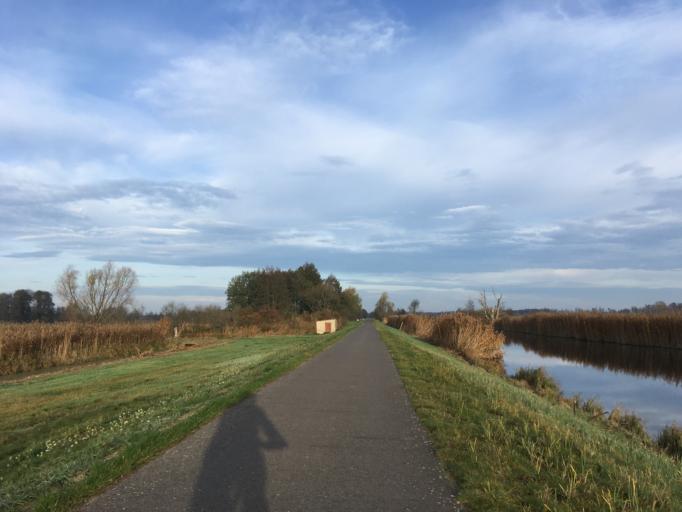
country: DE
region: Brandenburg
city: Lubbenau
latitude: 51.9048
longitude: 13.9275
